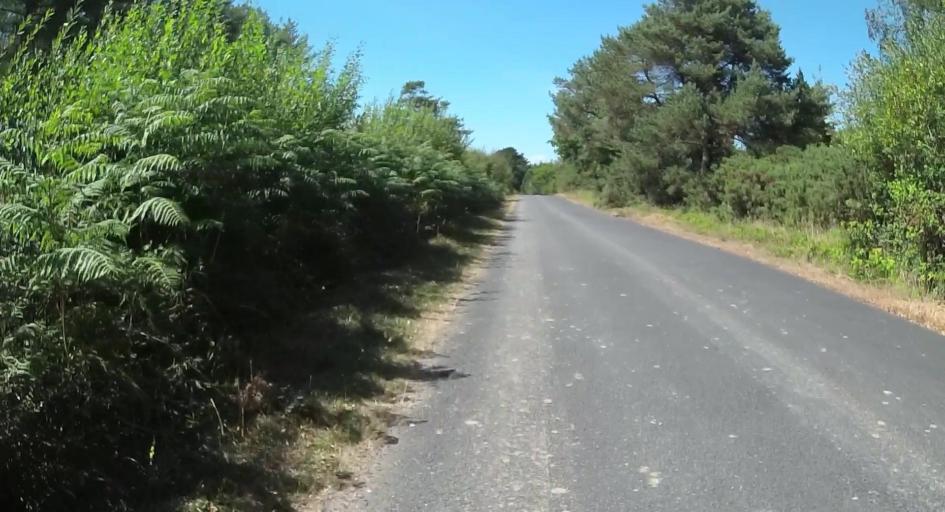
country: GB
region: England
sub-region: Dorset
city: Bovington Camp
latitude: 50.7280
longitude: -2.2564
